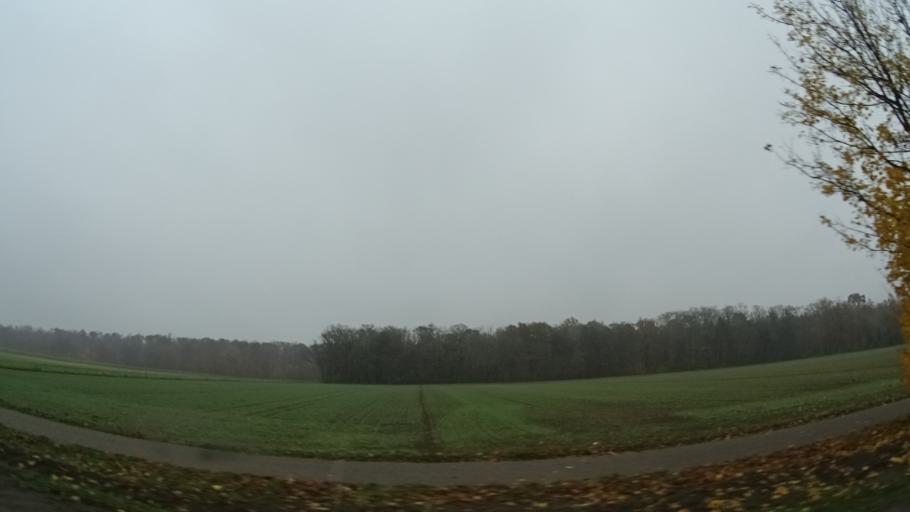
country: DE
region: Baden-Wuerttemberg
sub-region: Karlsruhe Region
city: Sankt Leon-Rot
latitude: 49.2822
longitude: 8.6277
